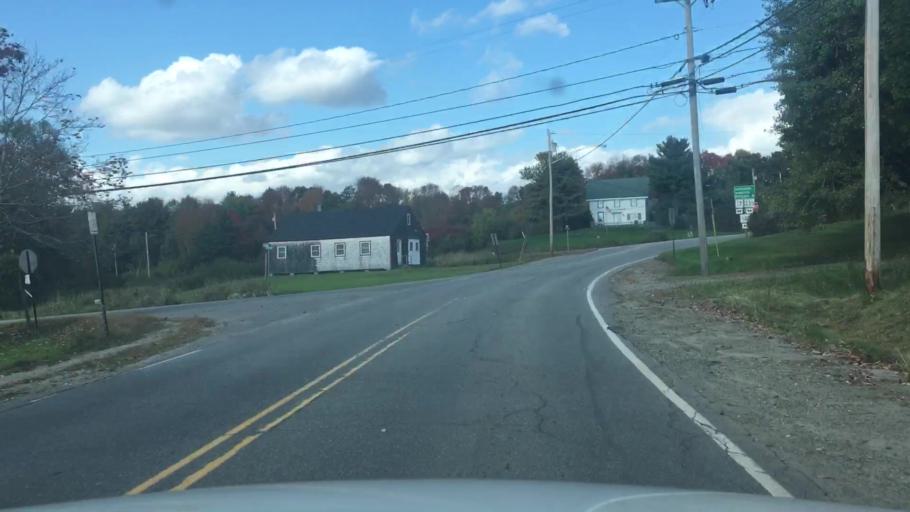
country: US
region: Maine
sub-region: Knox County
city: Union
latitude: 44.2121
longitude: -69.2637
